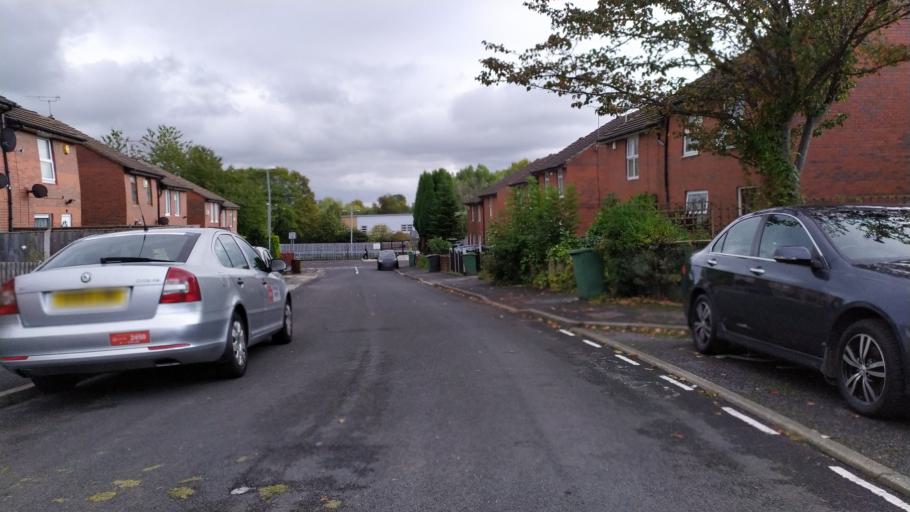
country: GB
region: England
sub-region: City and Borough of Leeds
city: Leeds
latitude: 53.8135
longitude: -1.5495
